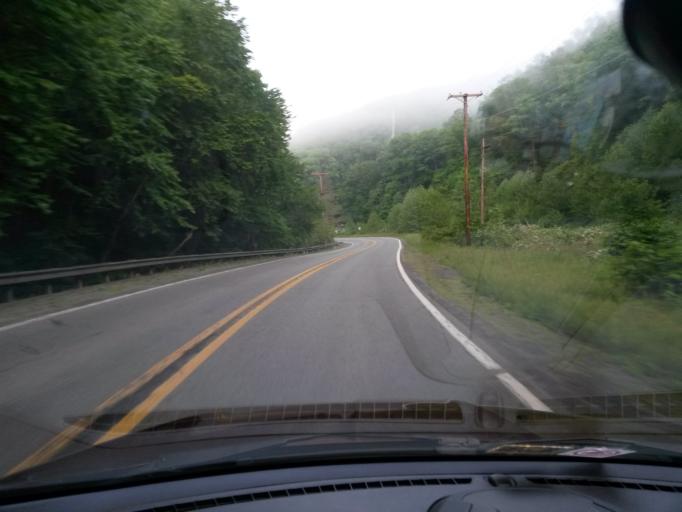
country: US
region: West Virginia
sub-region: McDowell County
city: Welch
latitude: 37.4484
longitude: -81.5463
